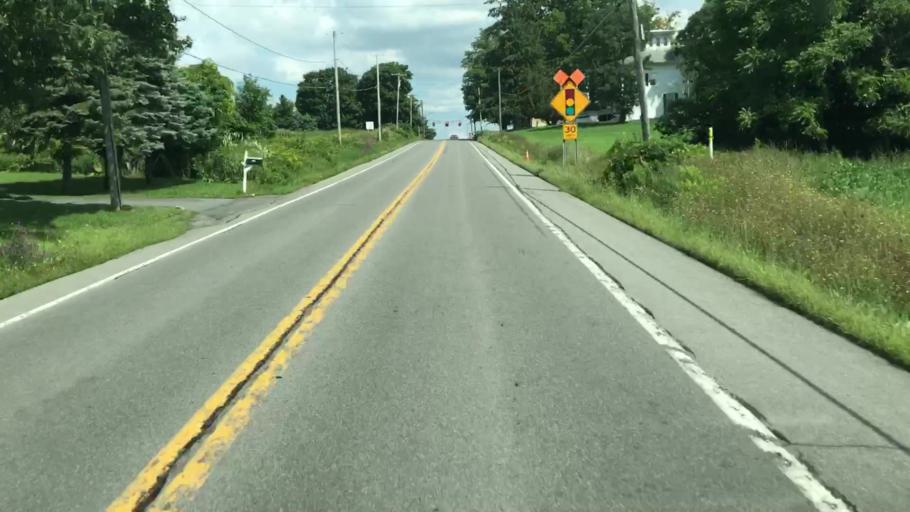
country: US
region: New York
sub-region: Onondaga County
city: Fairmount
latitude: 42.9860
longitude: -76.2628
